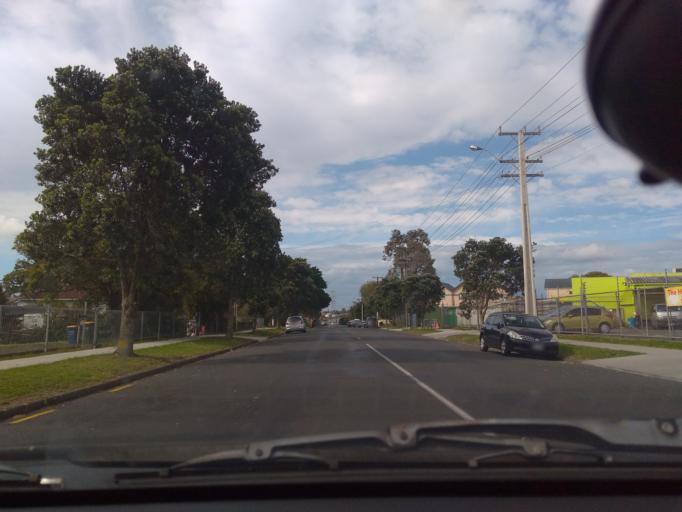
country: NZ
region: Auckland
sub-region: Auckland
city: Waitakere
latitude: -36.9061
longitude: 174.6833
